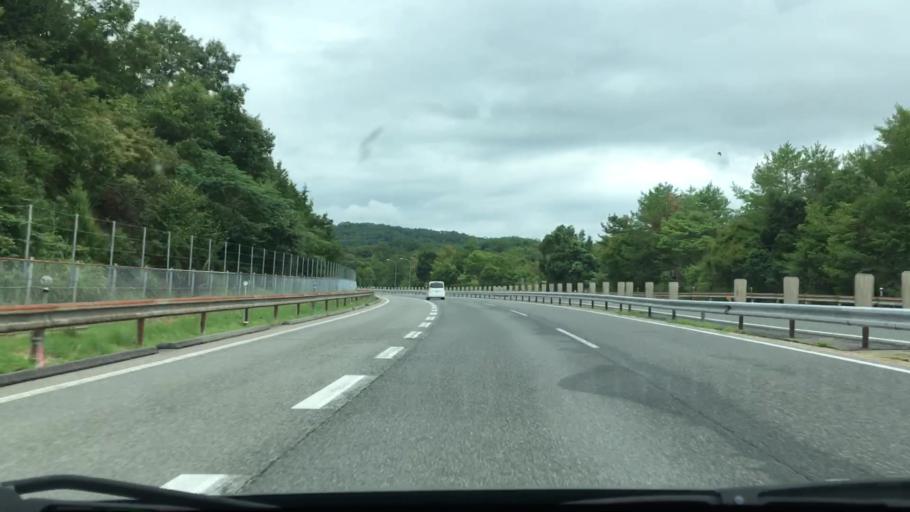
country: JP
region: Hiroshima
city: Miyoshi
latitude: 34.7563
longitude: 132.7574
